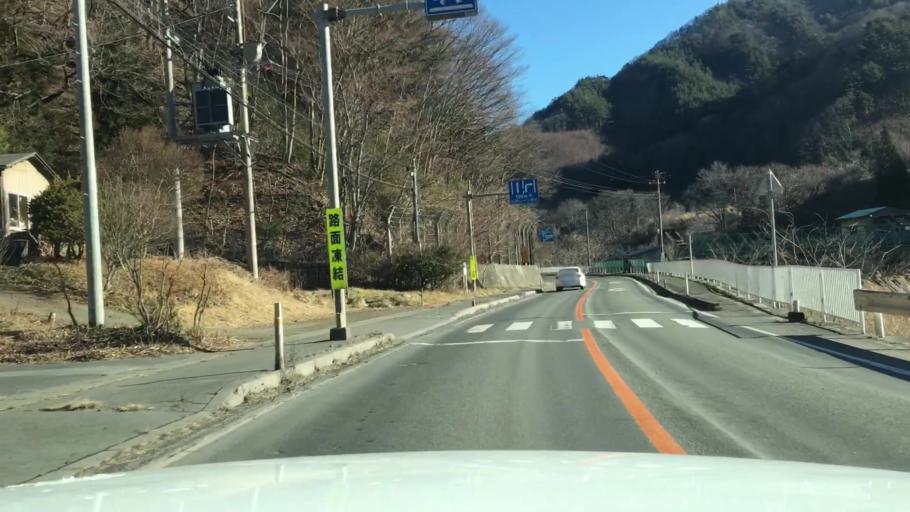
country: JP
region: Iwate
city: Miyako
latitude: 39.5928
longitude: 141.6728
